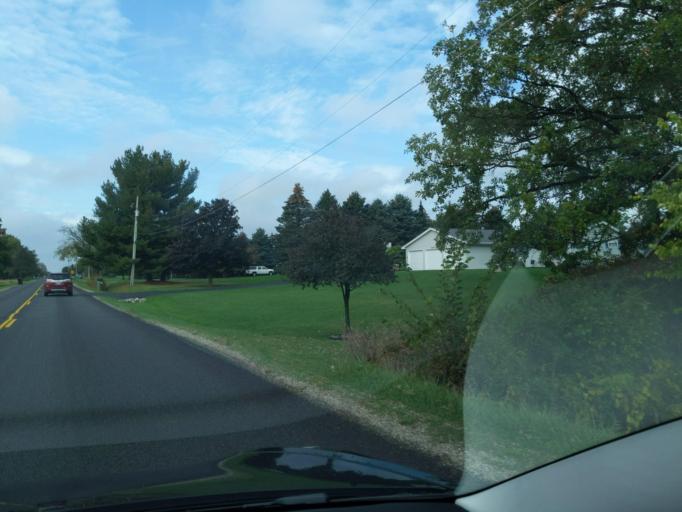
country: US
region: Michigan
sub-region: Eaton County
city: Dimondale
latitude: 42.6257
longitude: -84.6568
